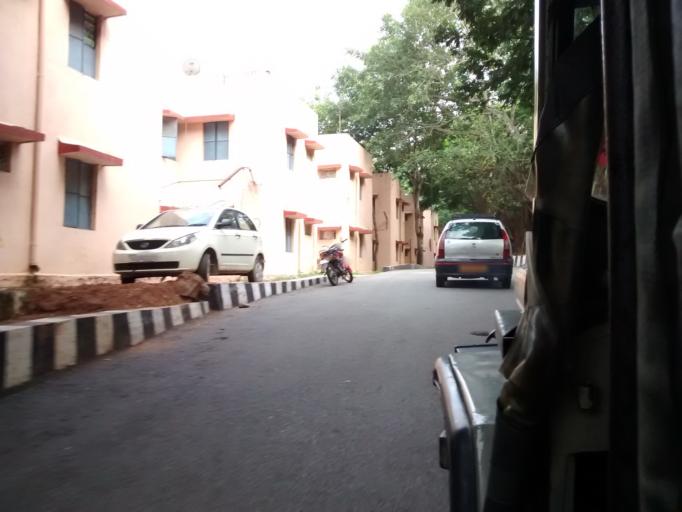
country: IN
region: Andhra Pradesh
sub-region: Chittoor
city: Tirumala
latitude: 13.6818
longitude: 79.3527
